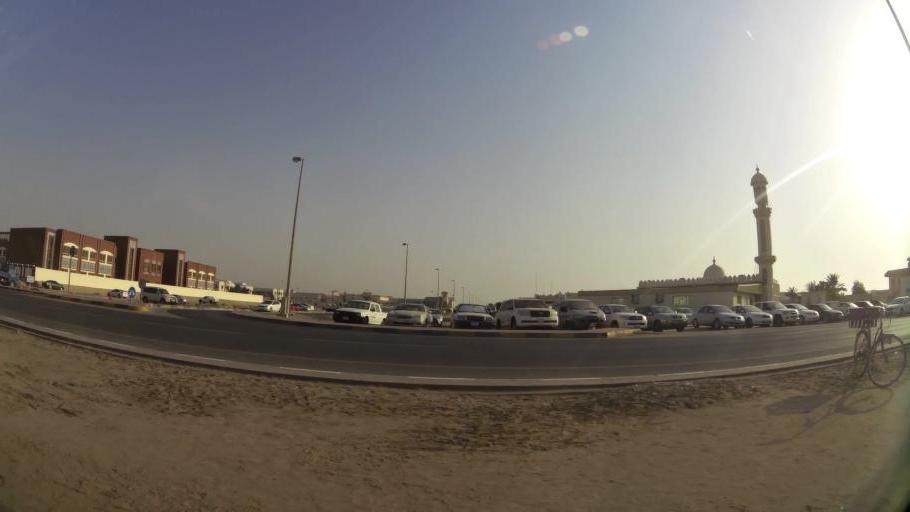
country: AE
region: Ajman
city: Ajman
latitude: 25.3818
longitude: 55.4476
